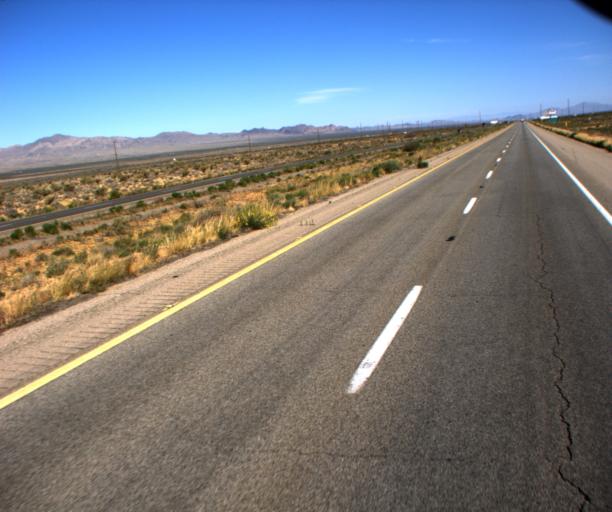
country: US
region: Arizona
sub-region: Mohave County
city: Dolan Springs
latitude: 35.5257
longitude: -114.3494
